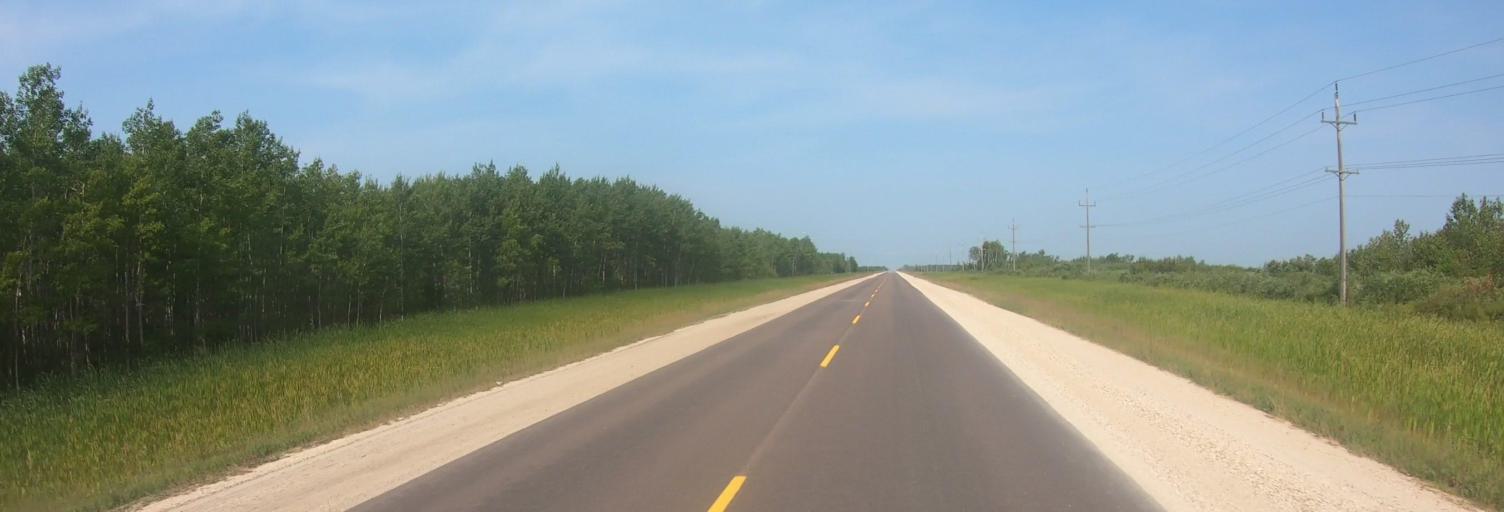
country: CA
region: Manitoba
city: La Broquerie
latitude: 49.2711
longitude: -96.4834
